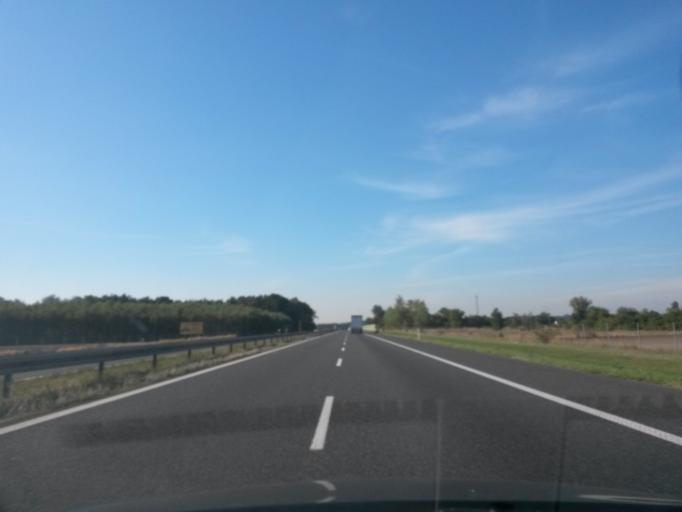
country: PL
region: Silesian Voivodeship
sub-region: Powiat gliwicki
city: Rudziniec
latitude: 50.3747
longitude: 18.4818
